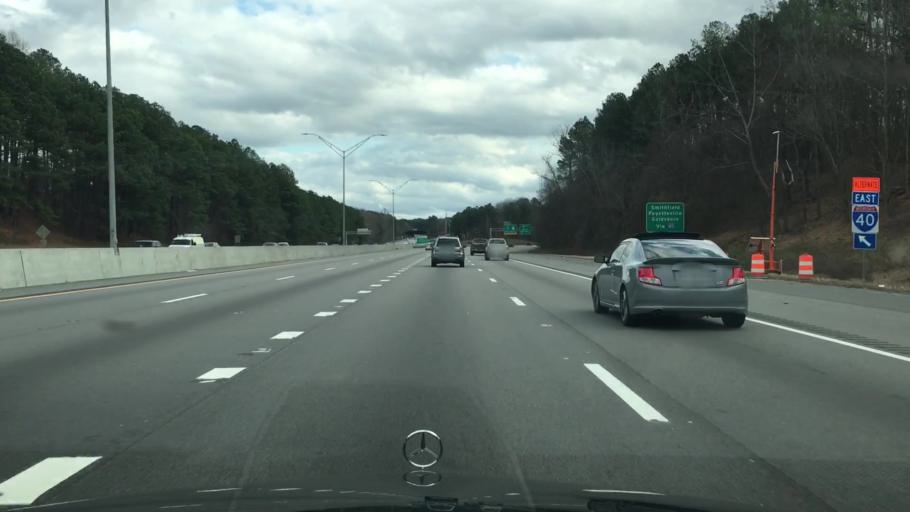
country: US
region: North Carolina
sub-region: Wake County
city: Raleigh
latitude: 35.7570
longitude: -78.6048
